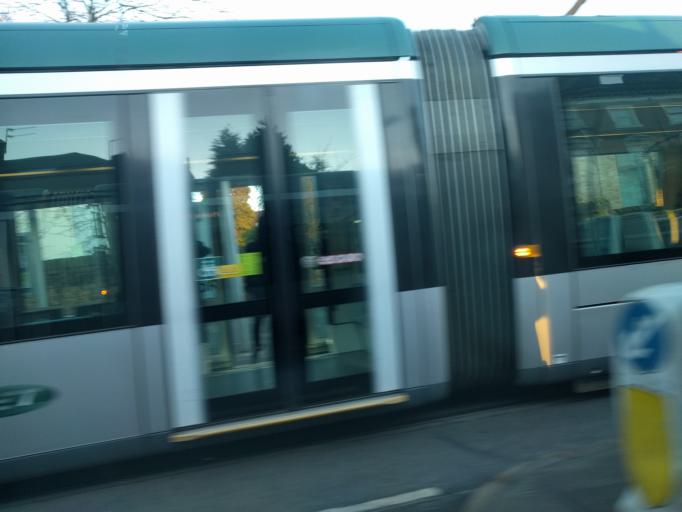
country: GB
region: England
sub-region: Nottingham
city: Nottingham
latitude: 52.9624
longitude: -1.1614
